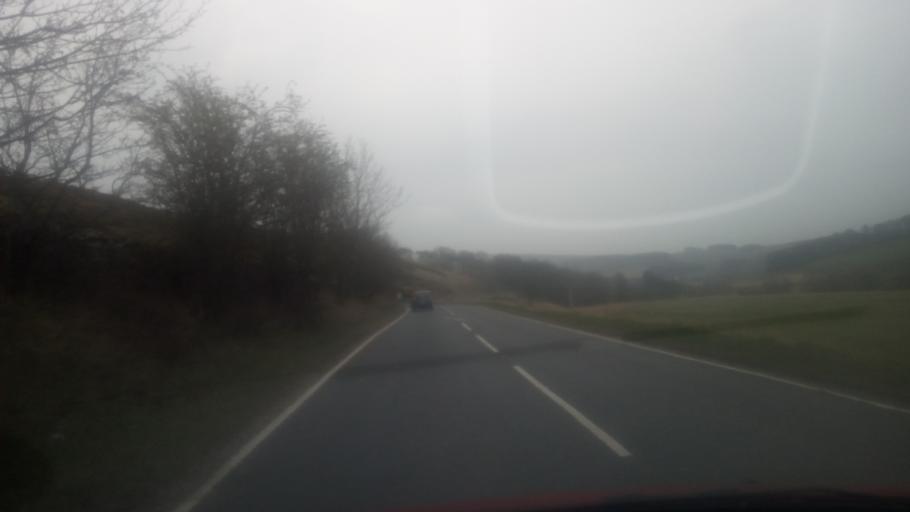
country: GB
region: Scotland
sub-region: The Scottish Borders
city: Galashiels
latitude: 55.7010
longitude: -2.8833
